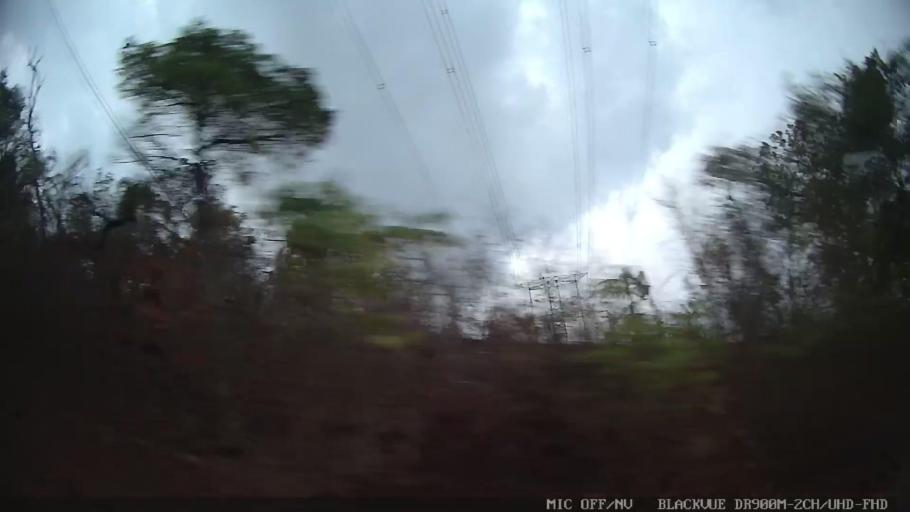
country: BR
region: Sao Paulo
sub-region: Braganca Paulista
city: Braganca Paulista
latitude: -22.9529
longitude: -46.6011
